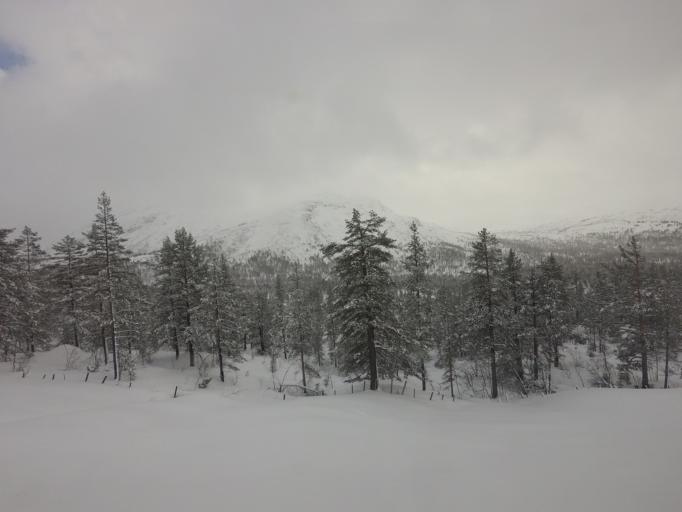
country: NO
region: Hordaland
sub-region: Ulvik
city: Ulvik
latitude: 60.7002
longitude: 6.8770
